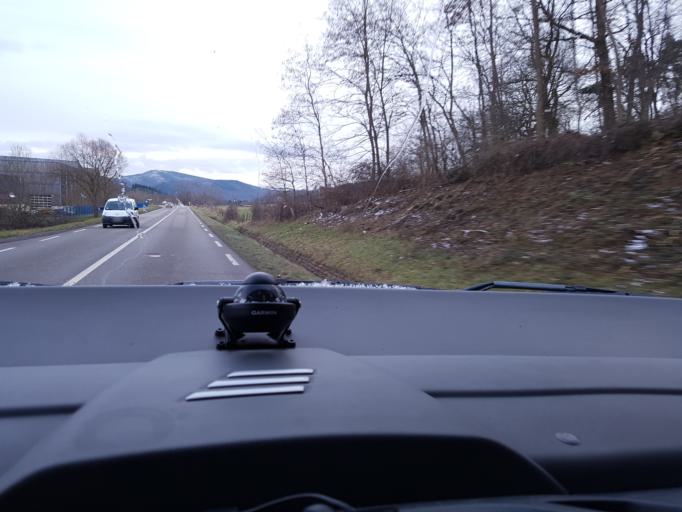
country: FR
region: Alsace
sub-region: Departement du Bas-Rhin
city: Ville
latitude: 48.3126
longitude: 7.3510
